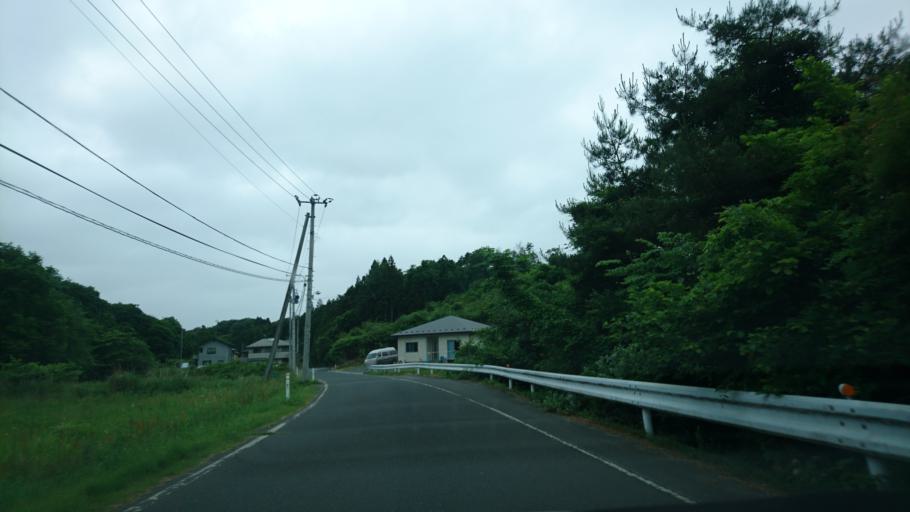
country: JP
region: Iwate
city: Ichinoseki
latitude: 38.9009
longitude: 141.1911
